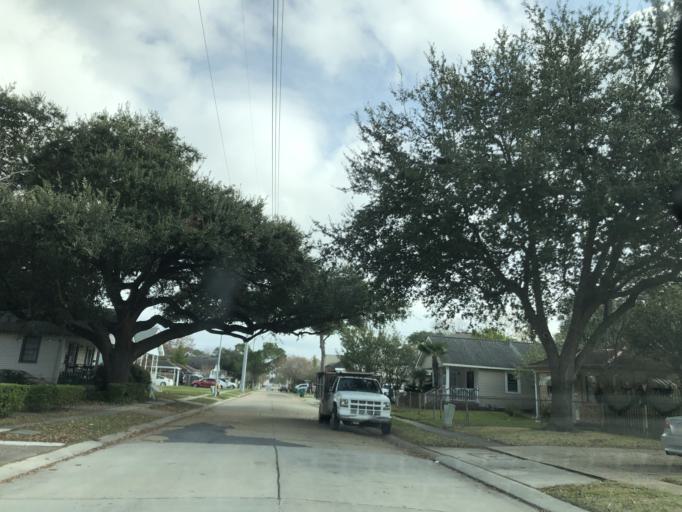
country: US
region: Louisiana
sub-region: Jefferson Parish
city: Metairie Terrace
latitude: 29.9768
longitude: -90.1640
